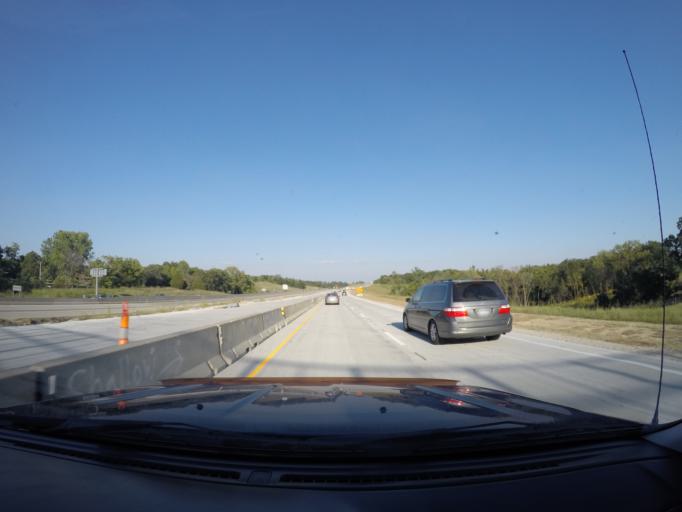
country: US
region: Kansas
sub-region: Wyandotte County
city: Bonner Springs
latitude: 39.1040
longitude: -94.8533
